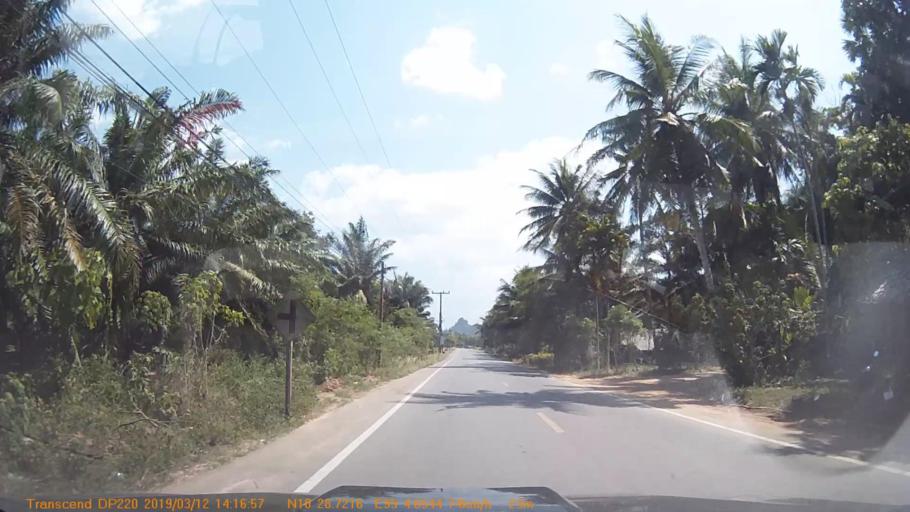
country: TH
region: Chumphon
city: Chumphon
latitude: 10.4784
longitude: 99.0776
